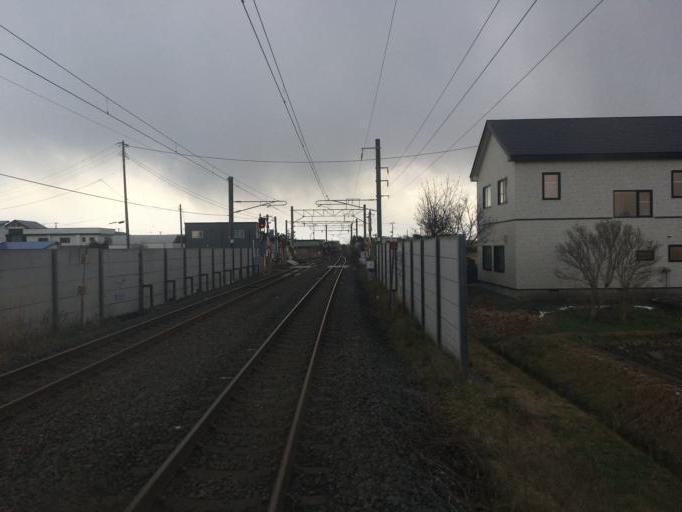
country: JP
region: Aomori
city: Aomori Shi
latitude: 40.9001
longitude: 140.6728
